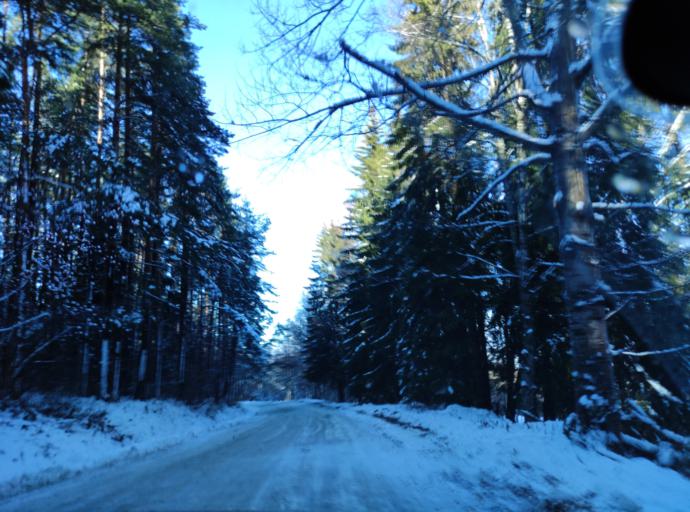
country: BG
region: Sofia-Capital
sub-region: Stolichna Obshtina
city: Sofia
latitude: 42.6018
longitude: 23.3027
